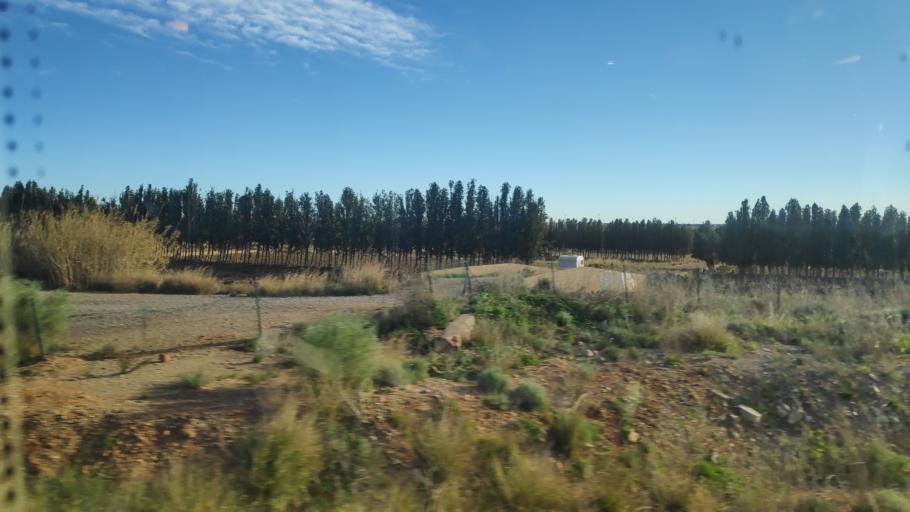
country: ES
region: Valencia
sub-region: Provincia de Castello
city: Benicassim
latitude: 40.0325
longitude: 0.0210
